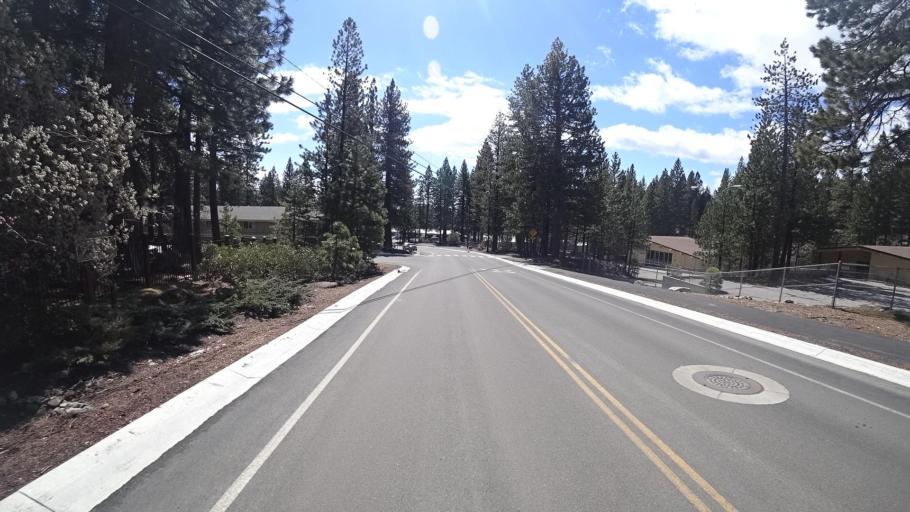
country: US
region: Nevada
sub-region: Washoe County
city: Incline Village
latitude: 39.2497
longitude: -119.9621
